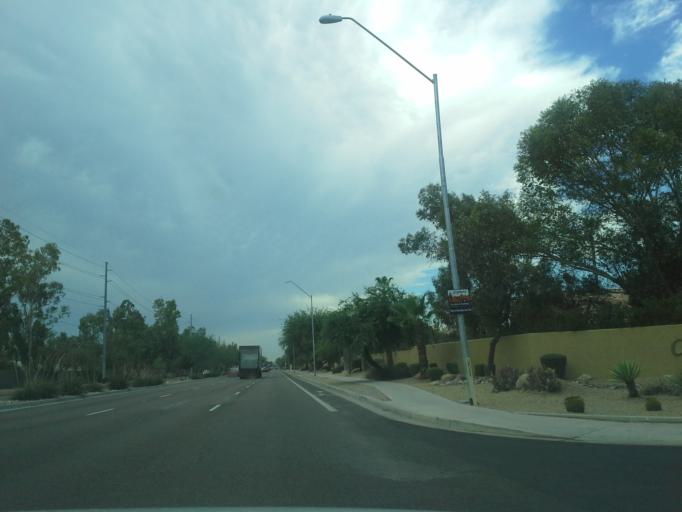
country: US
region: Arizona
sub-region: Maricopa County
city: Paradise Valley
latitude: 33.5731
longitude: -111.9262
